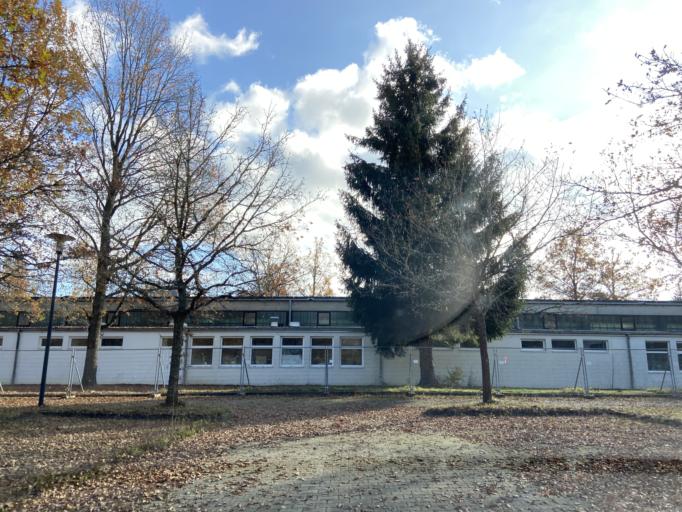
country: DE
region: Baden-Wuerttemberg
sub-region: Tuebingen Region
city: Sigmaringen
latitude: 48.0951
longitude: 9.2505
